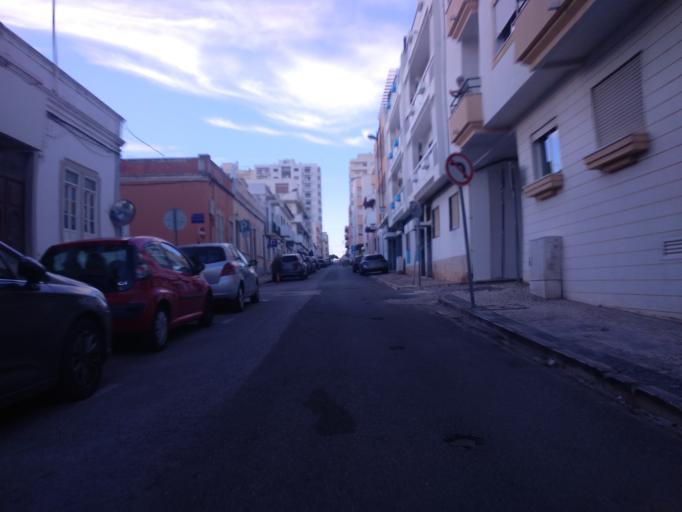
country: PT
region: Faro
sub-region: Faro
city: Faro
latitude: 37.0162
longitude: -7.9248
